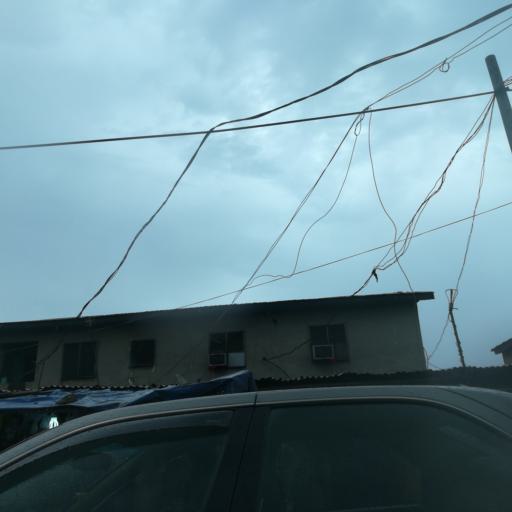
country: NG
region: Lagos
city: Oshodi
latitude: 6.5571
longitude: 3.3441
